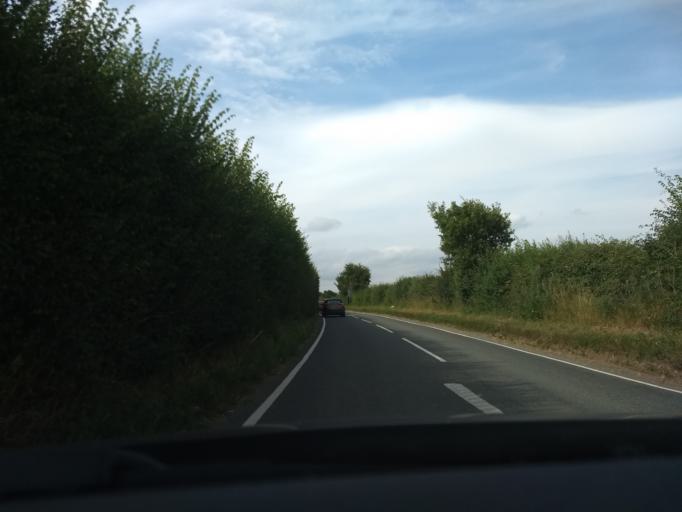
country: GB
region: England
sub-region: Suffolk
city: Ipswich
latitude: 52.0073
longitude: 1.1659
